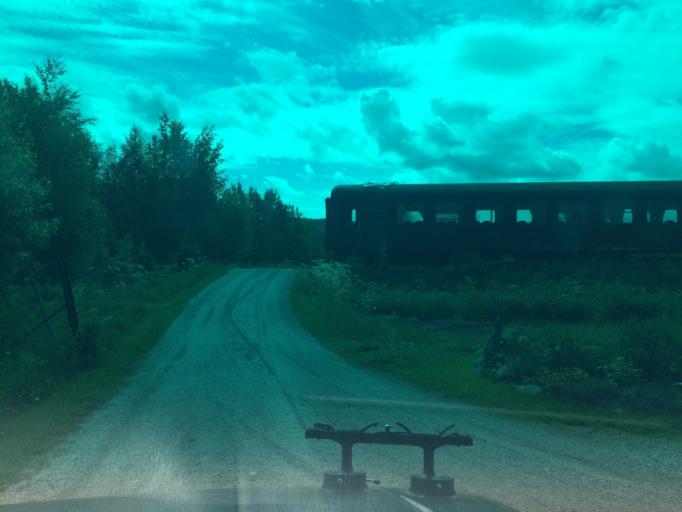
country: NO
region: Nord-Trondelag
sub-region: Overhalla
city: Ranemsletta
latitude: 64.4653
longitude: 12.0612
